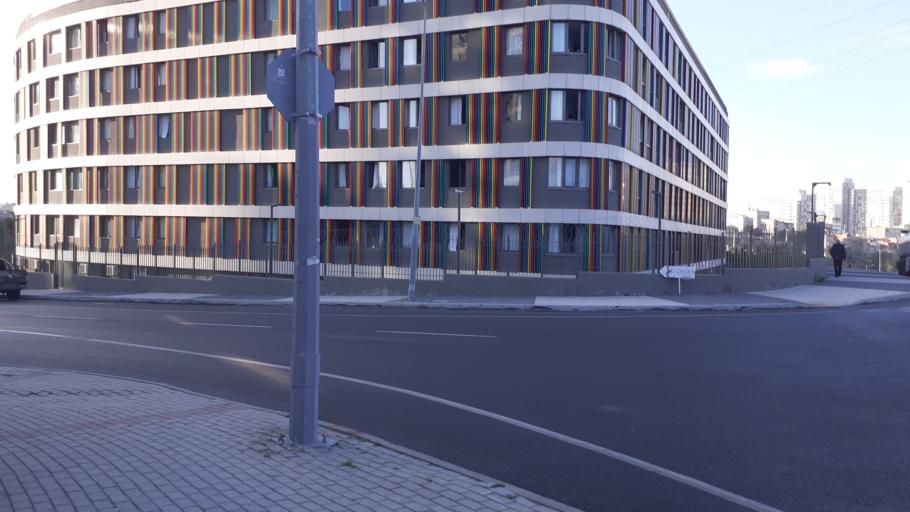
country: TR
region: Istanbul
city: Basaksehir
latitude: 41.0664
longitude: 28.7803
